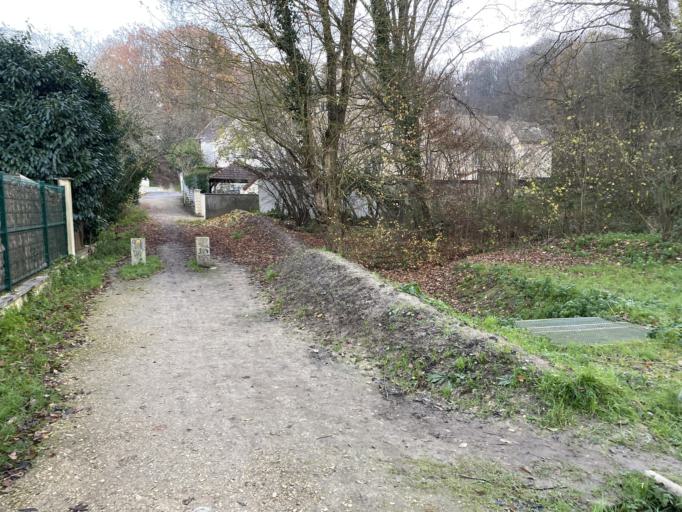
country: FR
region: Ile-de-France
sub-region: Departement de l'Essonne
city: Vauhallan
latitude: 48.7302
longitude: 2.2172
